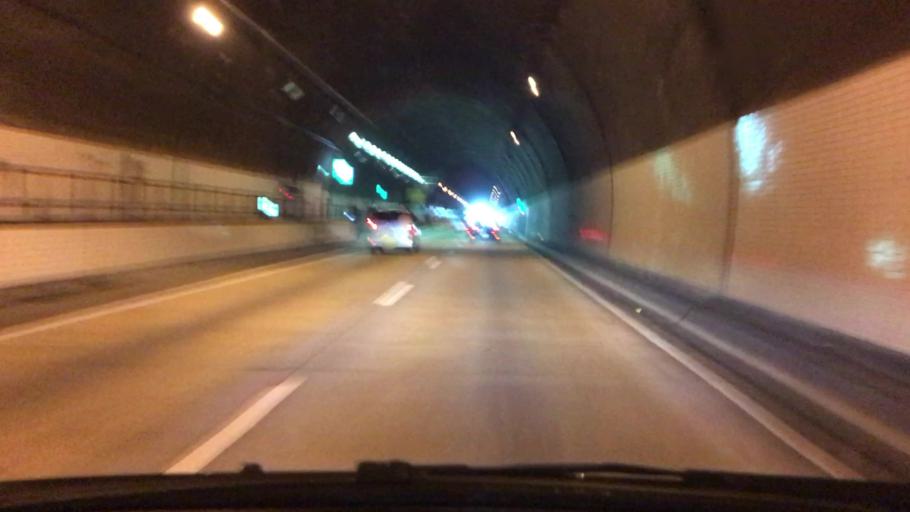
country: JP
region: Hyogo
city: Kobe
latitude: 34.7838
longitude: 135.2141
